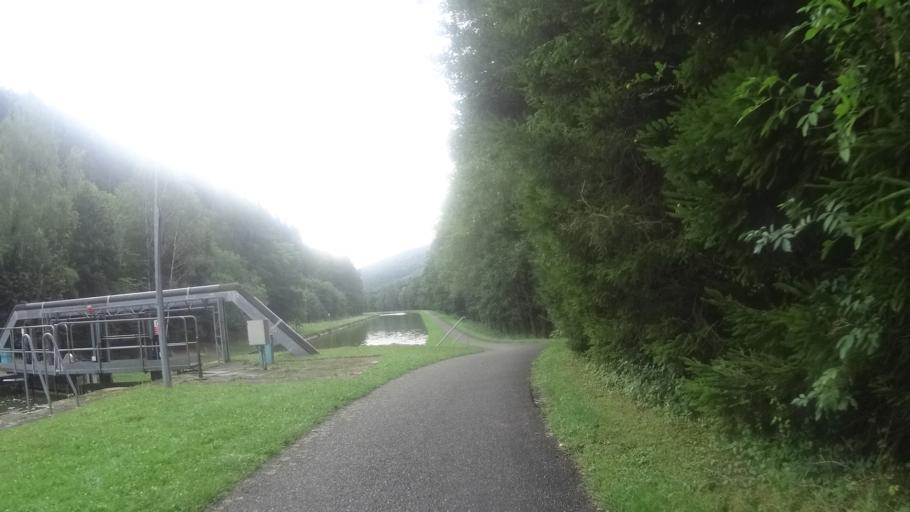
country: FR
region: Lorraine
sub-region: Departement de la Moselle
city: Phalsbourg
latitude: 48.7372
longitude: 7.2729
